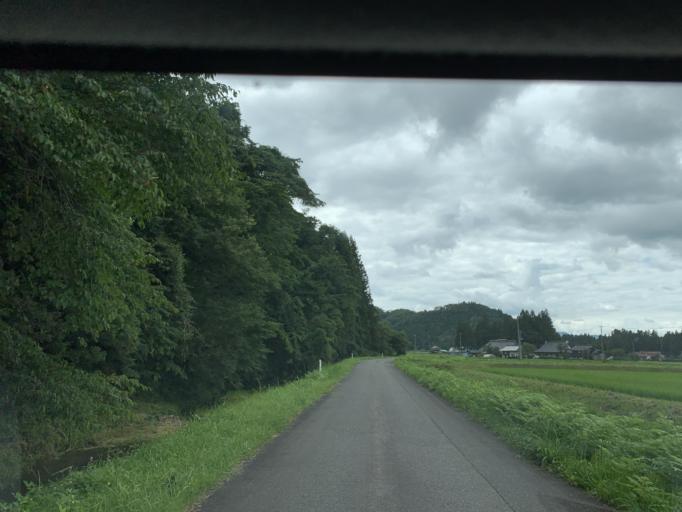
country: JP
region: Iwate
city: Ichinoseki
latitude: 38.9472
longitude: 141.0178
